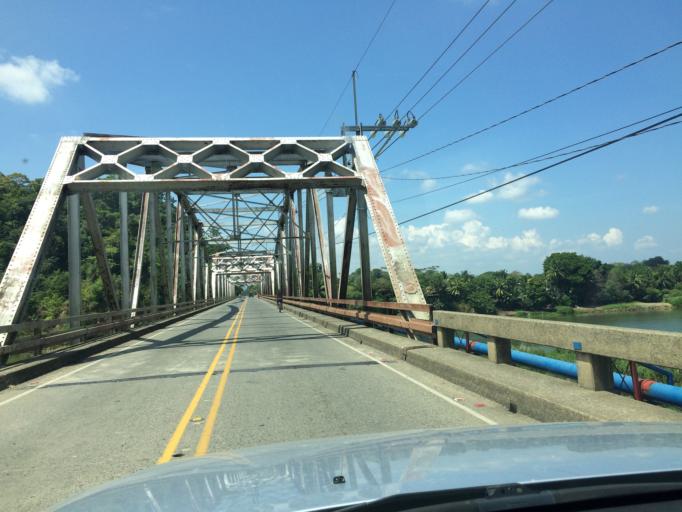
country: CR
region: Puntarenas
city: Ciudad Cortes
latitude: 8.9592
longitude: -83.4600
